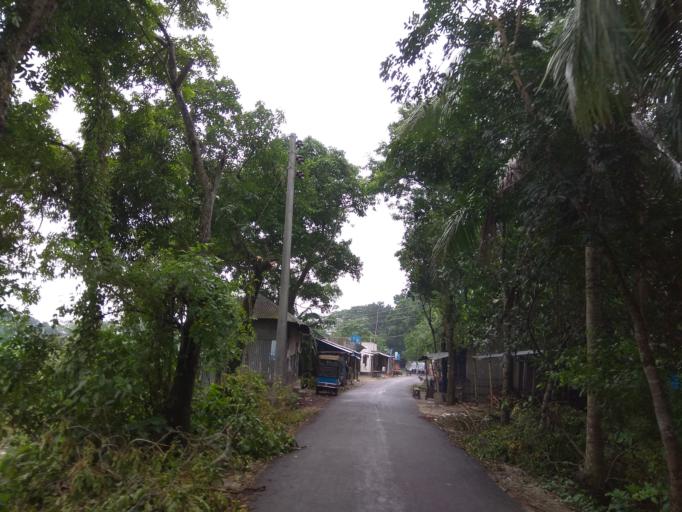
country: BD
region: Dhaka
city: Dohar
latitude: 23.4714
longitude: 90.0726
